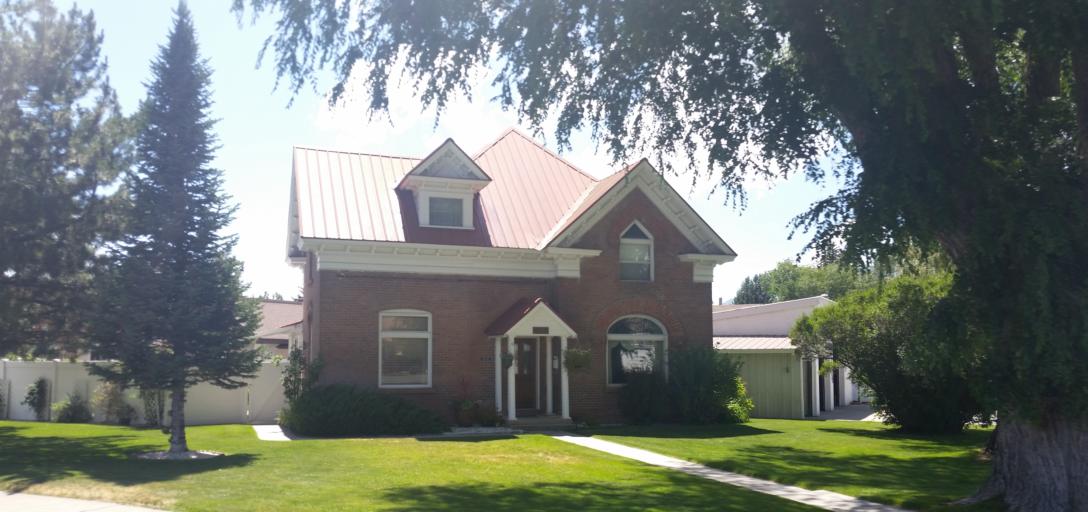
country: US
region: Utah
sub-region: Wasatch County
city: Heber
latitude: 40.5014
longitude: -111.4136
